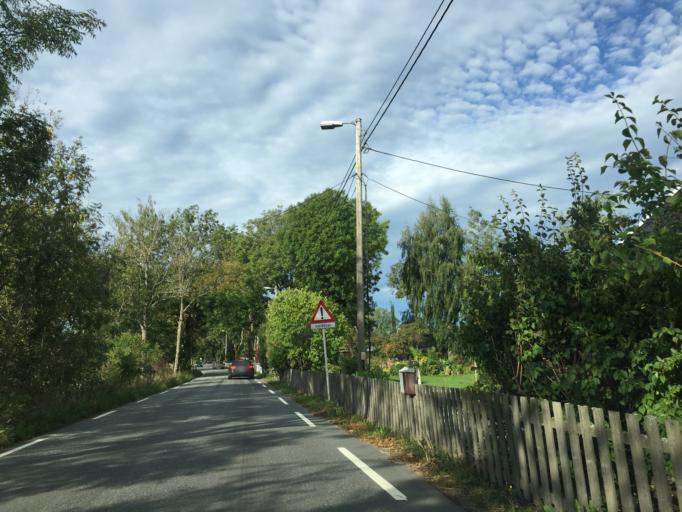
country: NO
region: Akershus
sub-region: As
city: As
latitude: 59.7060
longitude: 10.7684
